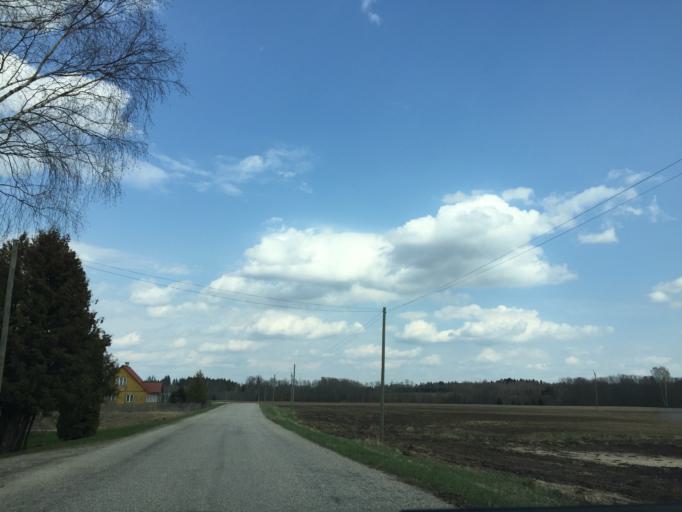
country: RU
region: Pskov
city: Pechory
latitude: 57.7164
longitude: 27.3230
